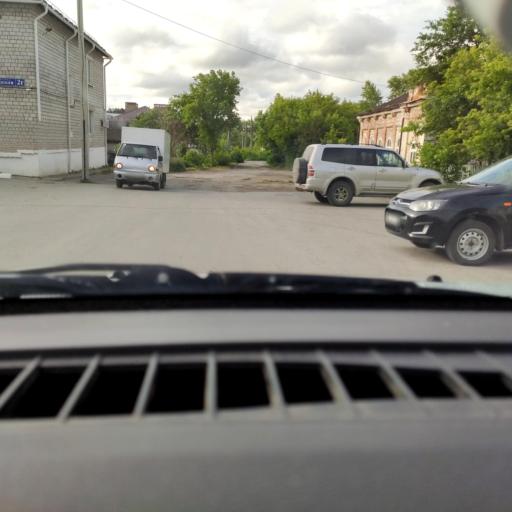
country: RU
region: Perm
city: Kungur
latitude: 57.4228
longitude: 56.9544
